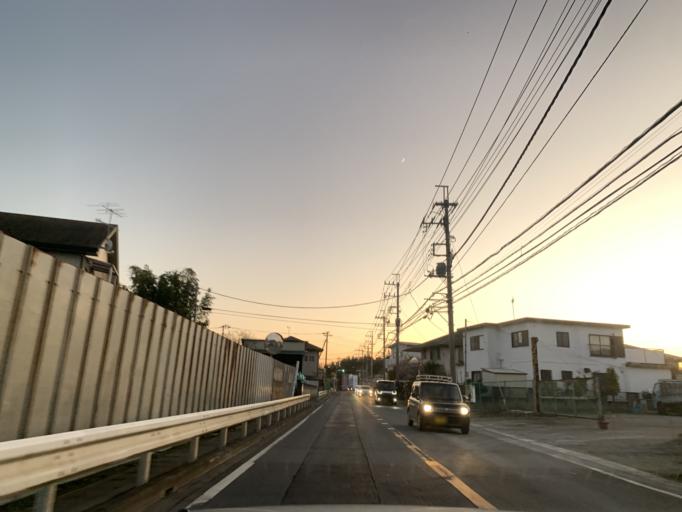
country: JP
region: Chiba
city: Nagareyama
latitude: 35.9055
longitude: 139.9023
